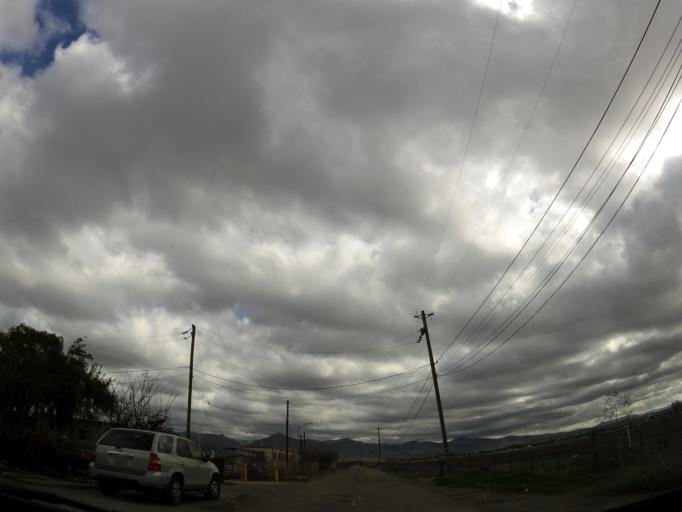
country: US
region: California
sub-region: San Benito County
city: Hollister
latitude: 36.8662
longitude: -121.3994
